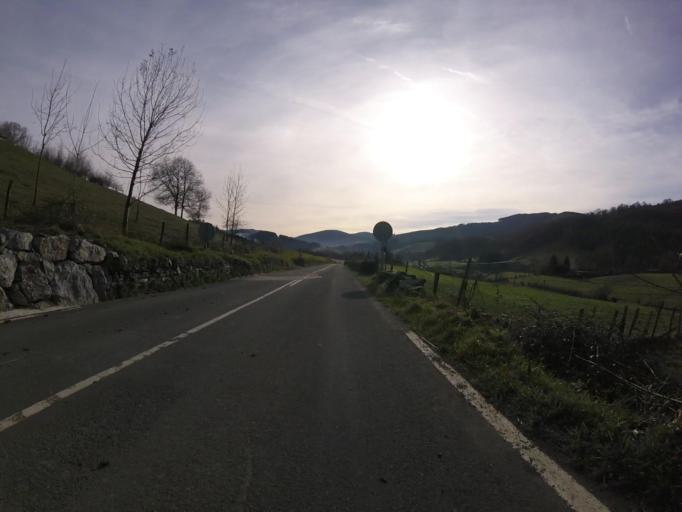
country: ES
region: Basque Country
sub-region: Provincia de Guipuzcoa
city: Berastegui
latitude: 43.1156
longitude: -1.9666
